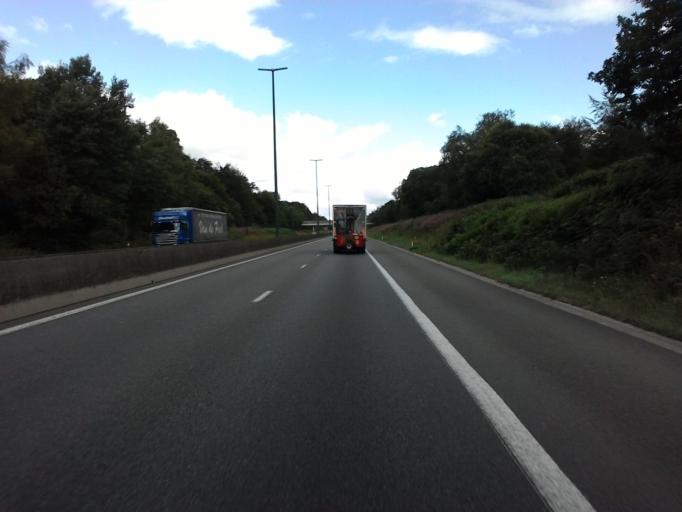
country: BE
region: Wallonia
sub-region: Province du Luxembourg
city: Habay-la-Vieille
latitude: 49.7360
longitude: 5.5768
